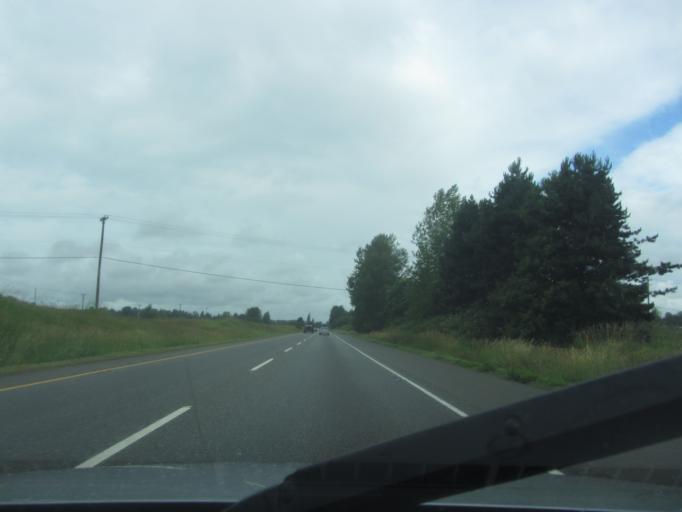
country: CA
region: British Columbia
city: Aldergrove
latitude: 49.0841
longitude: -122.4481
